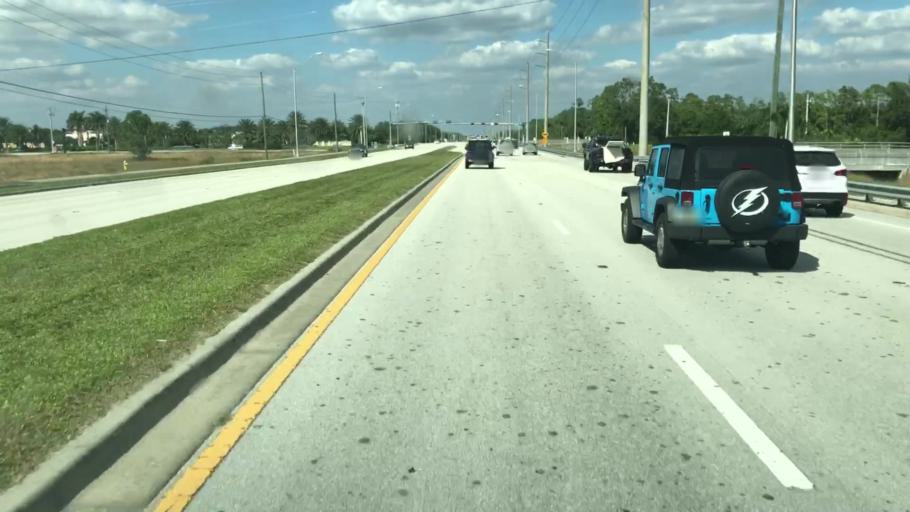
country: US
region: Florida
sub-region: Collier County
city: Vineyards
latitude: 26.2490
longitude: -81.6883
